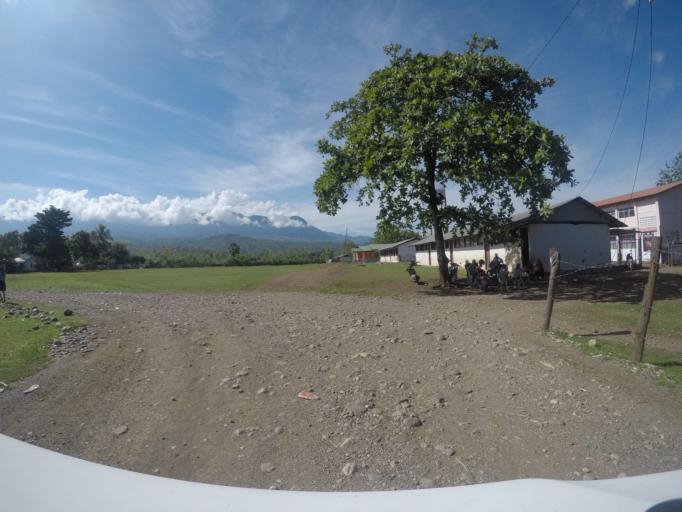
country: TL
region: Bobonaro
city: Maliana
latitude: -8.9919
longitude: 125.1988
